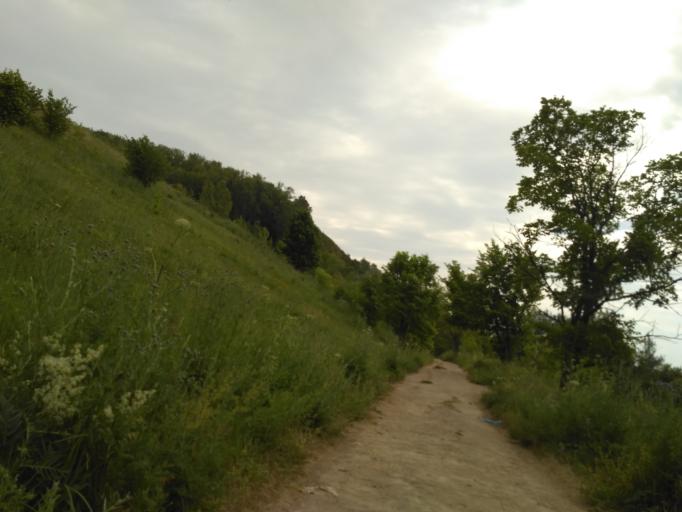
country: RU
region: Nizjnij Novgorod
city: Nizhniy Novgorod
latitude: 56.2778
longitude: 43.9712
